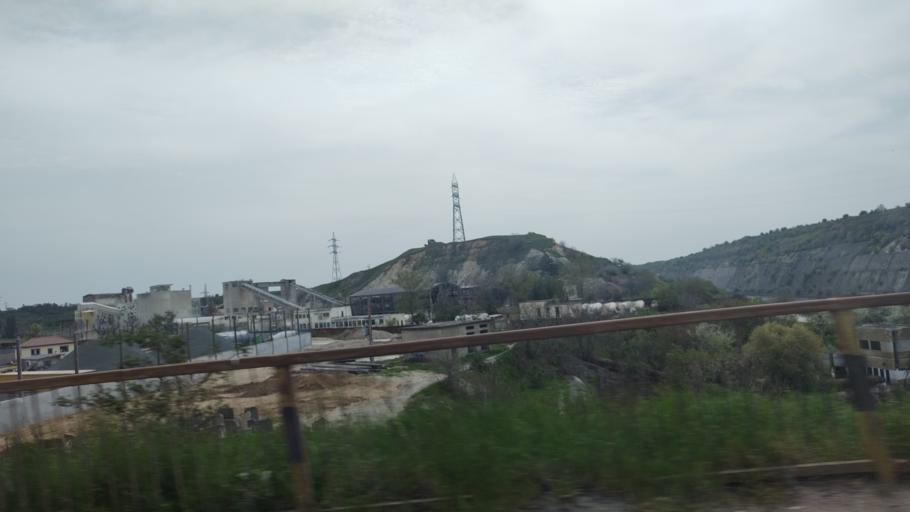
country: RO
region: Constanta
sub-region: Oras Murfatlar
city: Murfatlar
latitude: 44.1706
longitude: 28.4097
